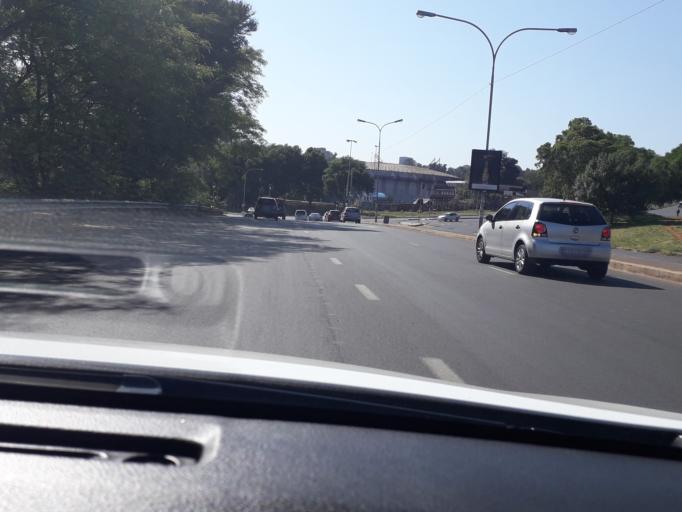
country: ZA
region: Gauteng
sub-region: City of Johannesburg Metropolitan Municipality
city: Johannesburg
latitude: -26.1864
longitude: 28.0164
